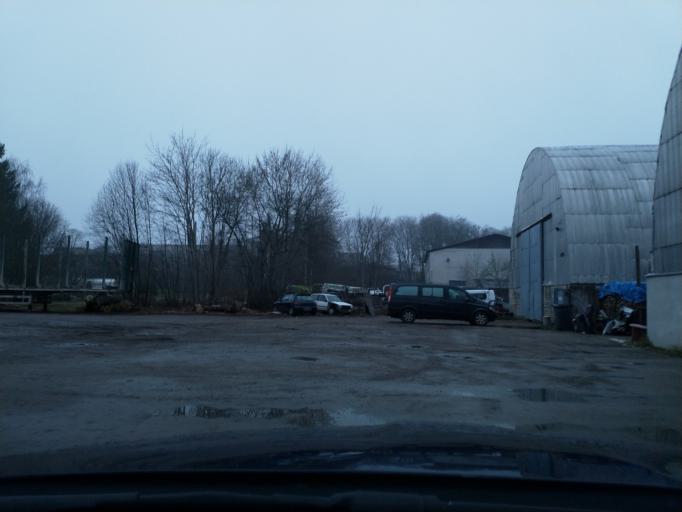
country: LV
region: Kuldigas Rajons
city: Kuldiga
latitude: 56.9796
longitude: 21.9666
